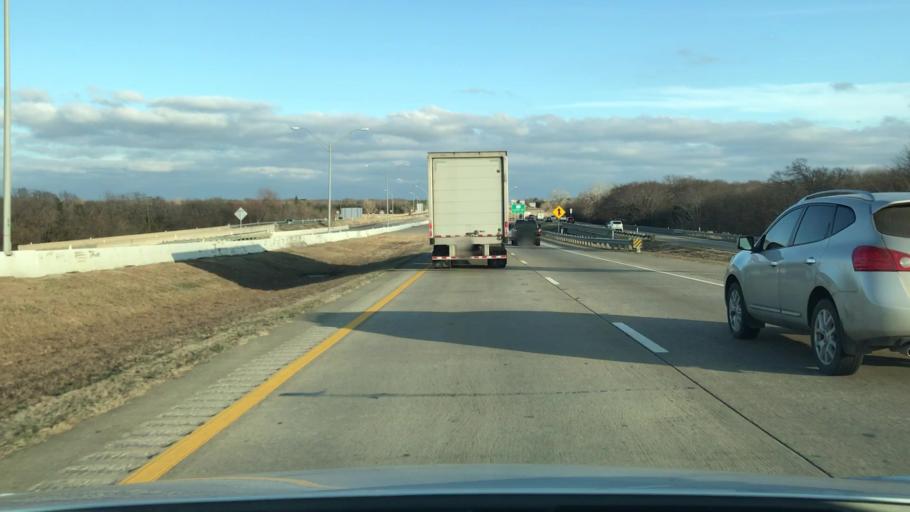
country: US
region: Texas
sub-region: Dallas County
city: Mesquite
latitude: 32.7902
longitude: -96.5945
